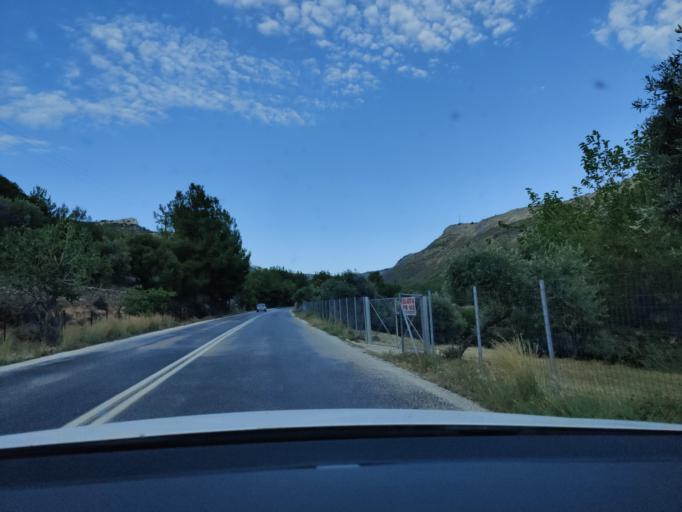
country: GR
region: East Macedonia and Thrace
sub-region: Nomos Kavalas
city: Limenaria
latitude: 40.6169
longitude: 24.6411
